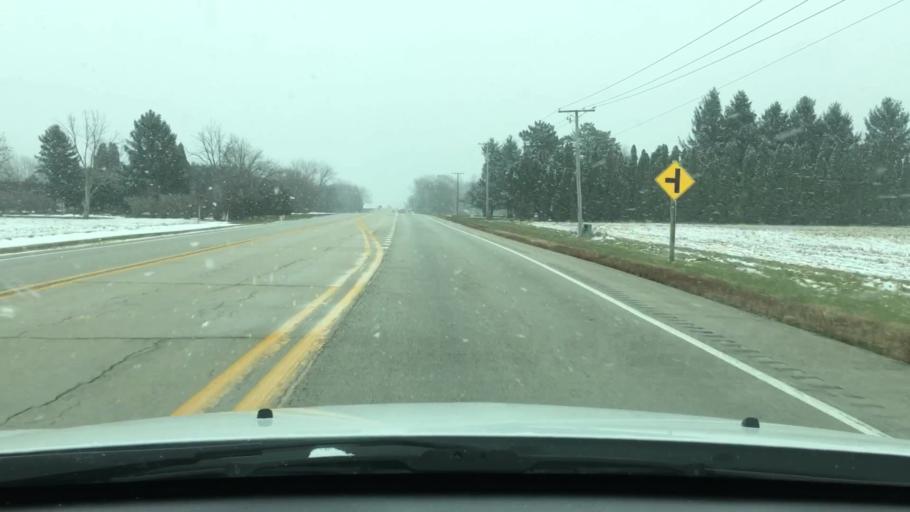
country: US
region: Illinois
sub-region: DeKalb County
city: Malta
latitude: 41.9360
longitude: -88.8298
